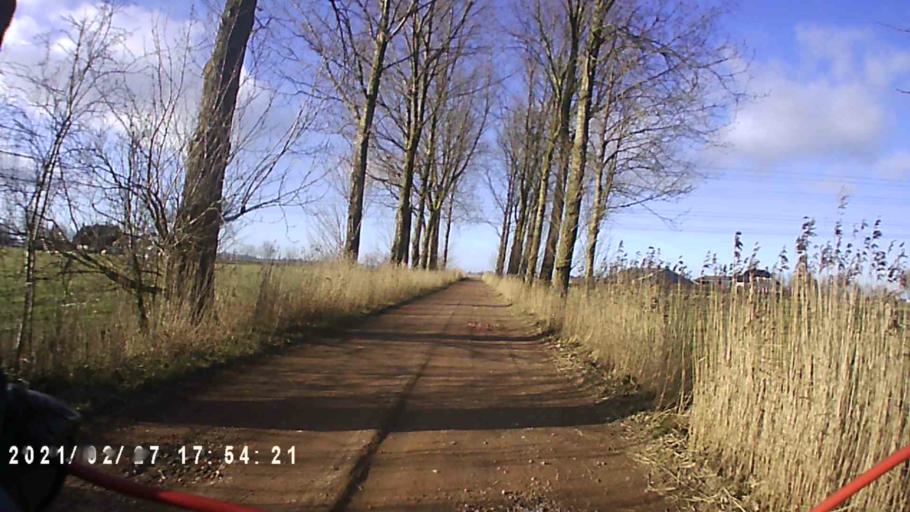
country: NL
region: Groningen
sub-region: Gemeente Bedum
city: Bedum
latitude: 53.3129
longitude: 6.6162
